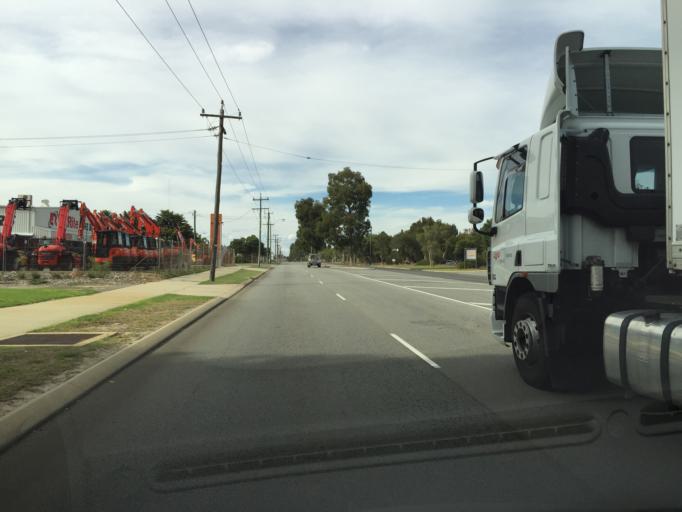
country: AU
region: Western Australia
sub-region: Canning
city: Willetton
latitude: -32.0676
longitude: 115.8981
